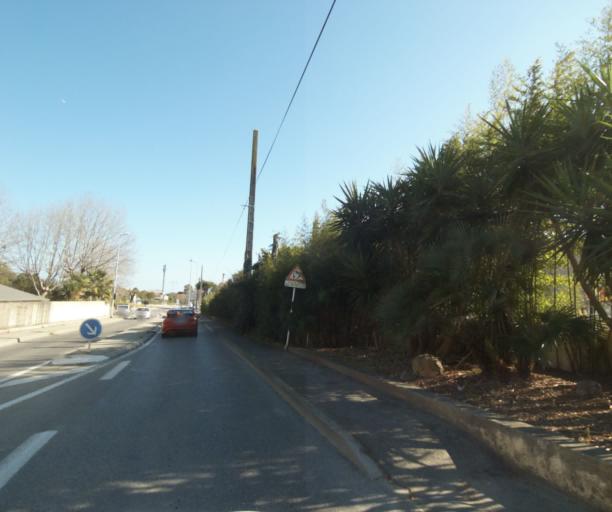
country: FR
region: Provence-Alpes-Cote d'Azur
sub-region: Departement des Alpes-Maritimes
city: Biot
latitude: 43.6150
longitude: 7.1186
